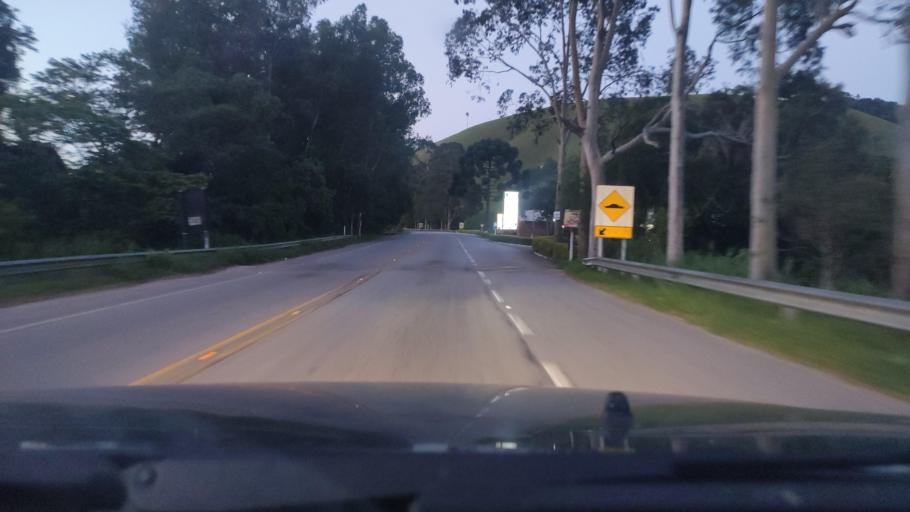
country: BR
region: Sao Paulo
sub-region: Campos Do Jordao
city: Campos do Jordao
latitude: -22.7234
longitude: -45.7268
